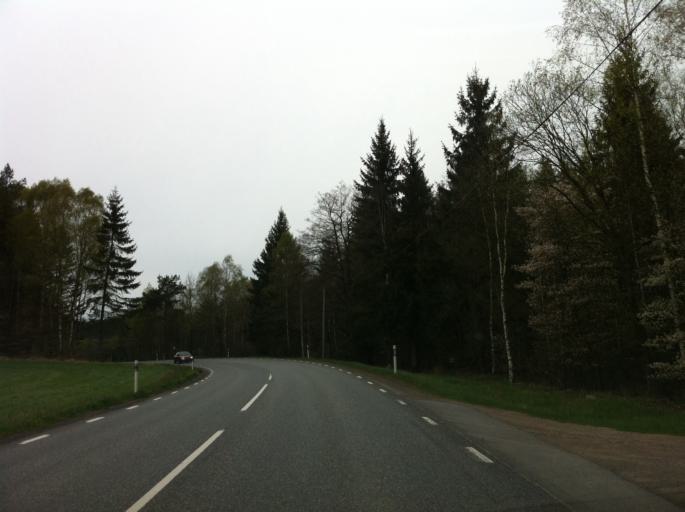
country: SE
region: Halland
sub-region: Falkenbergs Kommun
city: Falkenberg
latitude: 57.0586
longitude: 12.6282
